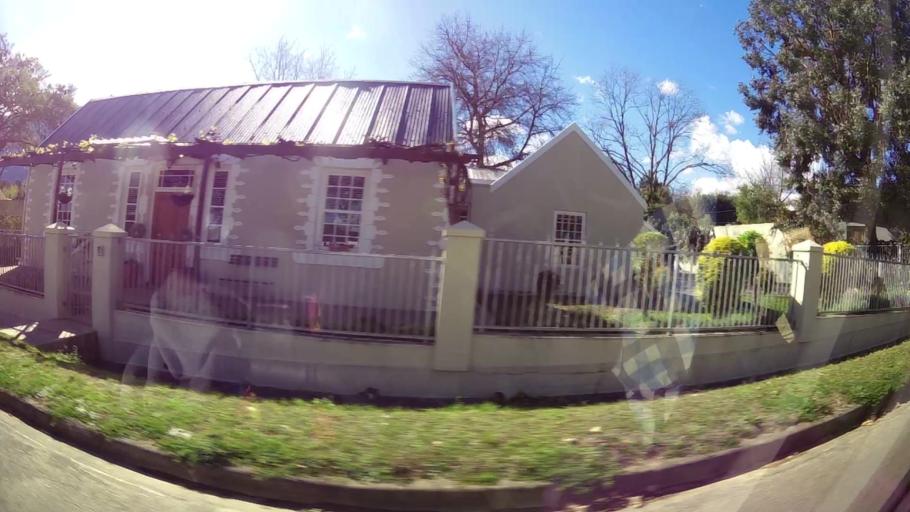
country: ZA
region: Western Cape
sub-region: Overberg District Municipality
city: Swellendam
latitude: -34.0208
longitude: 20.4504
